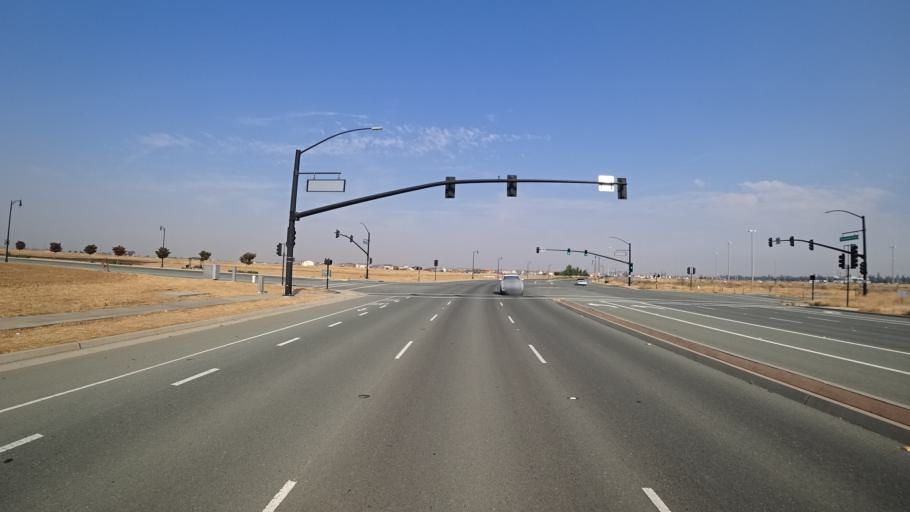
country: US
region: California
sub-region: Sacramento County
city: Elk Grove
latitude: 38.3762
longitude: -121.3707
